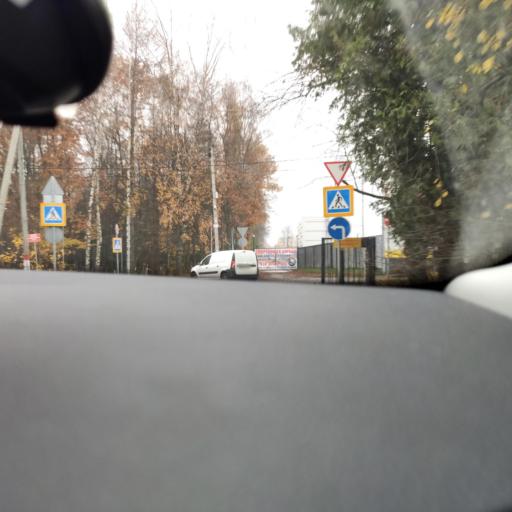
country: RU
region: Moskovskaya
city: Dedovsk
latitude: 55.8569
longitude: 37.1312
